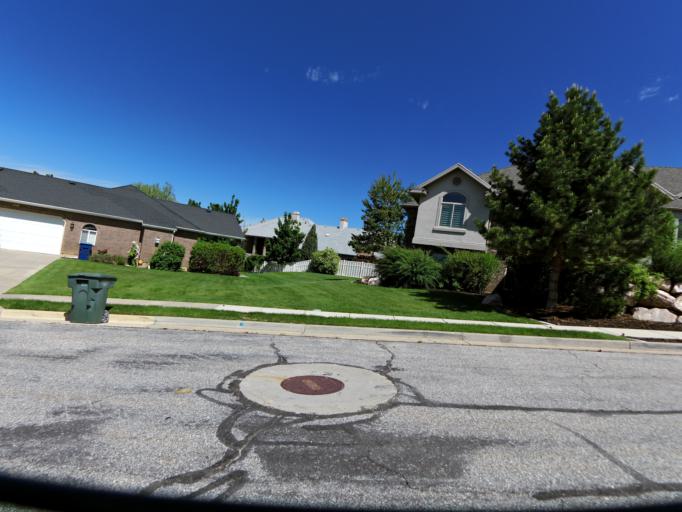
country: US
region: Utah
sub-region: Weber County
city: South Ogden
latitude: 41.1767
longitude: -111.9406
